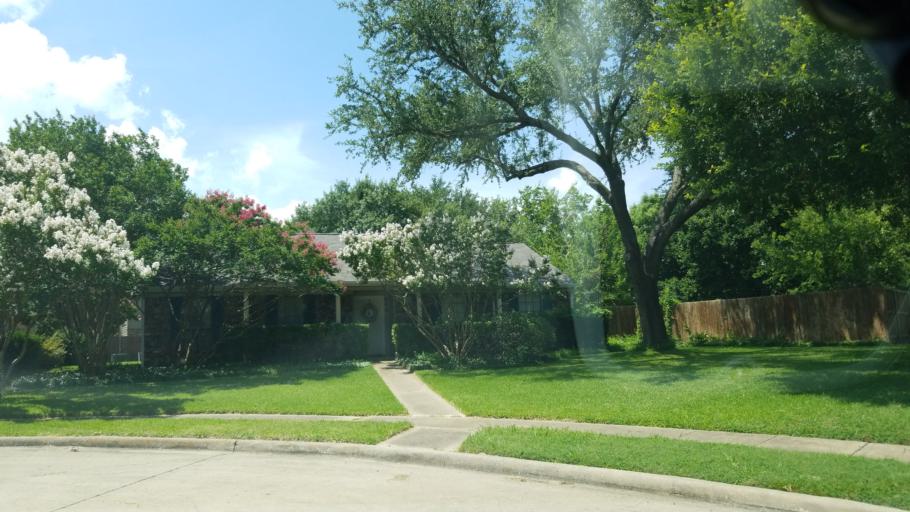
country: US
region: Texas
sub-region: Dallas County
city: Coppell
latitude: 32.9650
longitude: -96.9660
